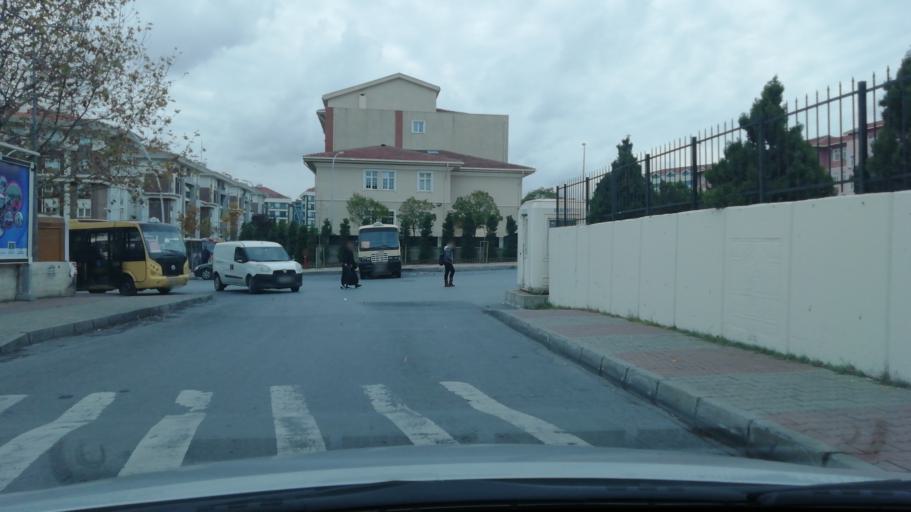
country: TR
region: Istanbul
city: Bahcelievler
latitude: 41.0164
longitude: 28.8287
